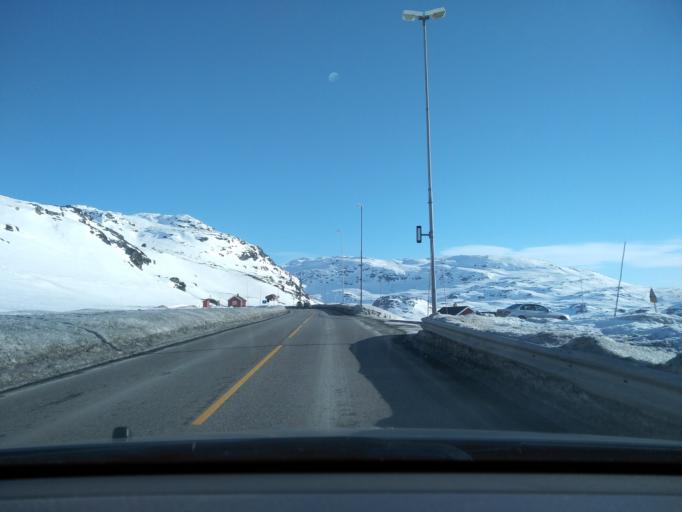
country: NO
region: Aust-Agder
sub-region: Bykle
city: Hovden
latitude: 59.8403
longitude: 6.9842
